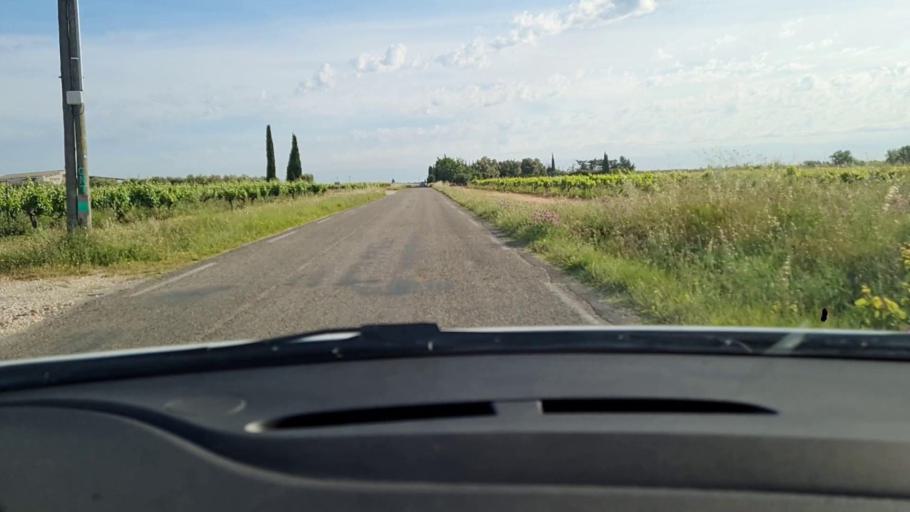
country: FR
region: Languedoc-Roussillon
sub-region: Departement du Gard
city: Bellegarde
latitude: 43.7682
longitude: 4.5157
